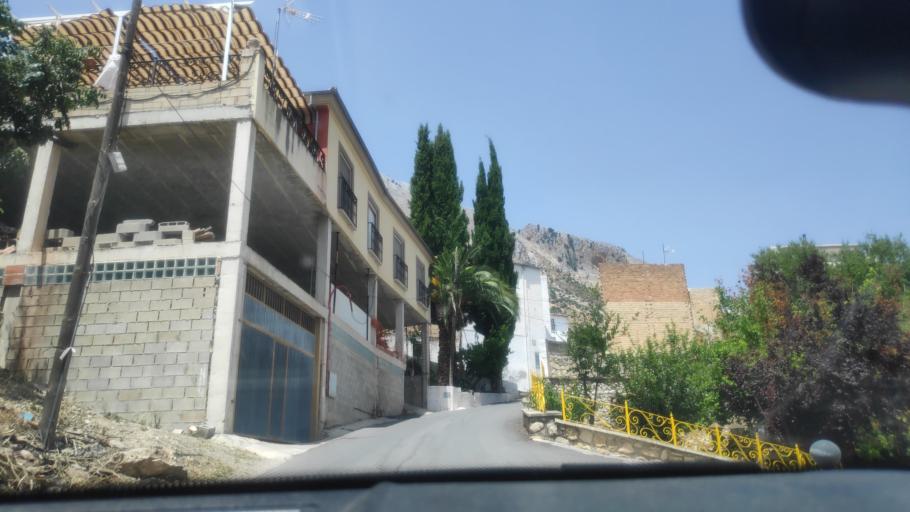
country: ES
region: Andalusia
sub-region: Provincia de Jaen
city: Torres
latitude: 37.7937
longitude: -3.4648
